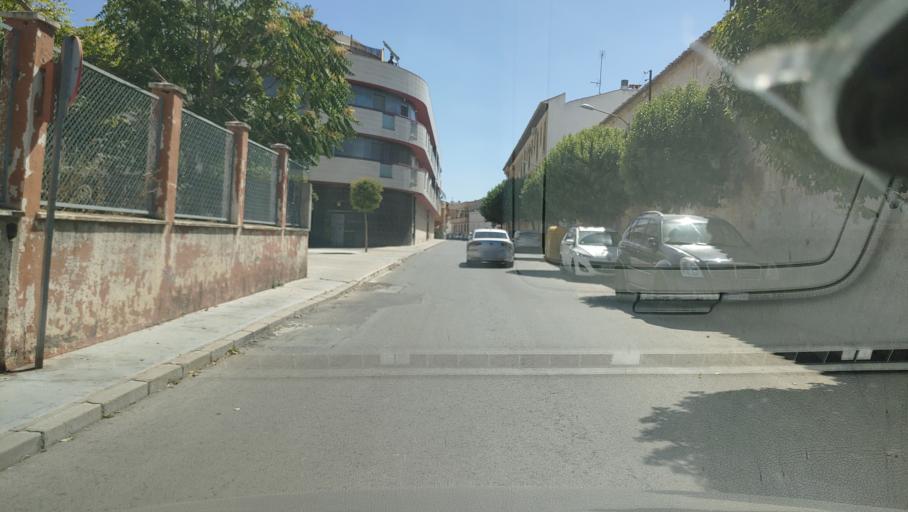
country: ES
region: Castille-La Mancha
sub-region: Provincia de Ciudad Real
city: Valdepenas
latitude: 38.7670
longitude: -3.3829
